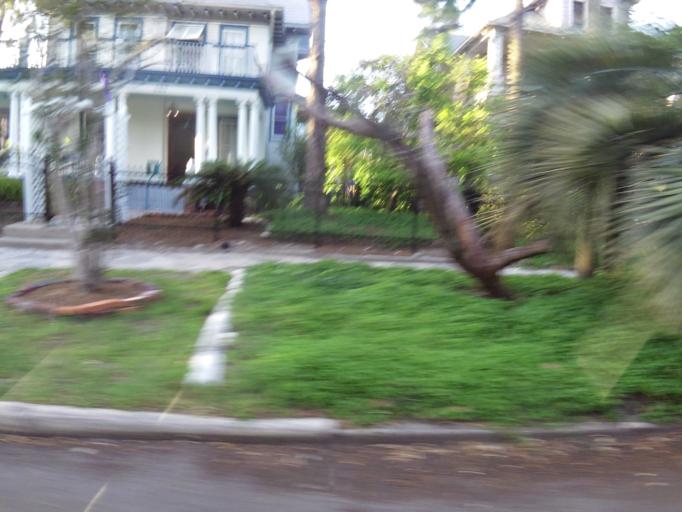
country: US
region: Florida
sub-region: Duval County
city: Jacksonville
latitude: 30.3394
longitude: -81.6575
